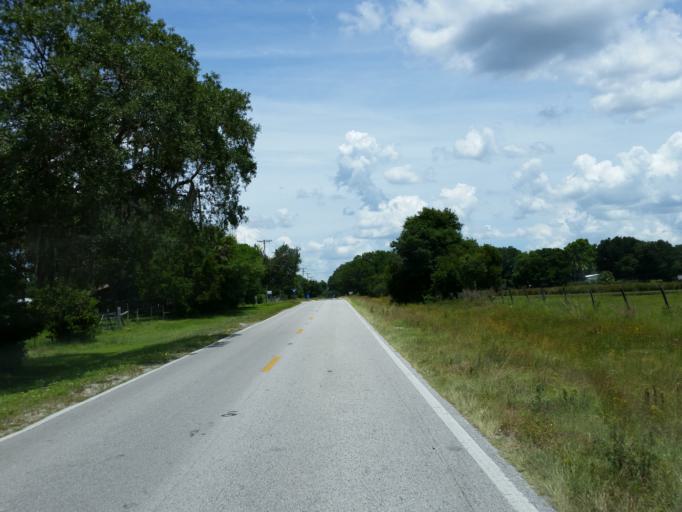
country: US
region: Florida
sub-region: Hillsborough County
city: Dover
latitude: 28.0471
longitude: -82.2265
